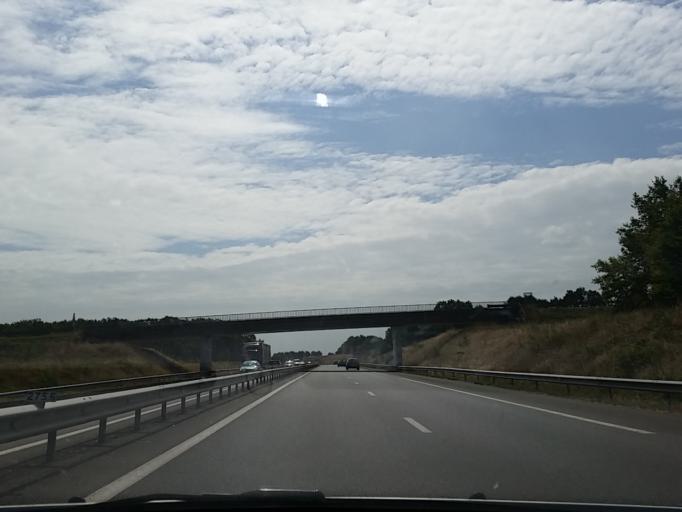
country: FR
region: Auvergne
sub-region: Departement de l'Allier
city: Vallon-en-Sully
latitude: 46.5221
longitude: 2.5732
